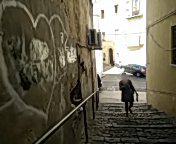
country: IT
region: Sicily
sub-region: Palermo
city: Castelbuono
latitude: 37.9301
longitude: 14.0893
